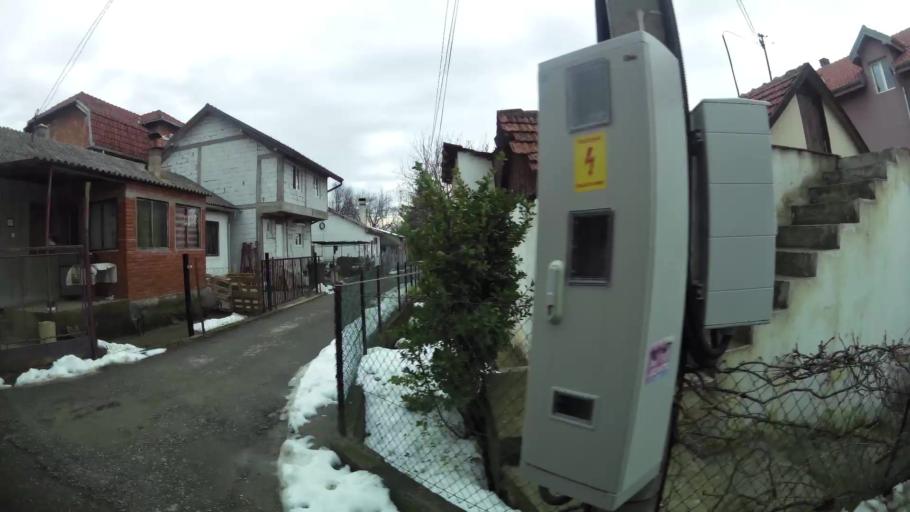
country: RS
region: Central Serbia
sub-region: Belgrade
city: Rakovica
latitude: 44.7426
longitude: 20.3951
